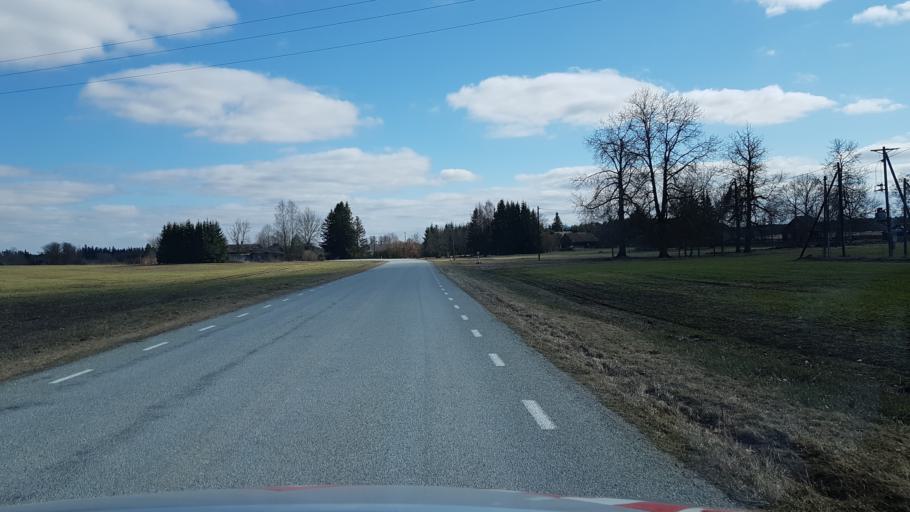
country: EE
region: Laeaene-Virumaa
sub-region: Tapa vald
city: Tapa
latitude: 59.2529
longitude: 25.7375
